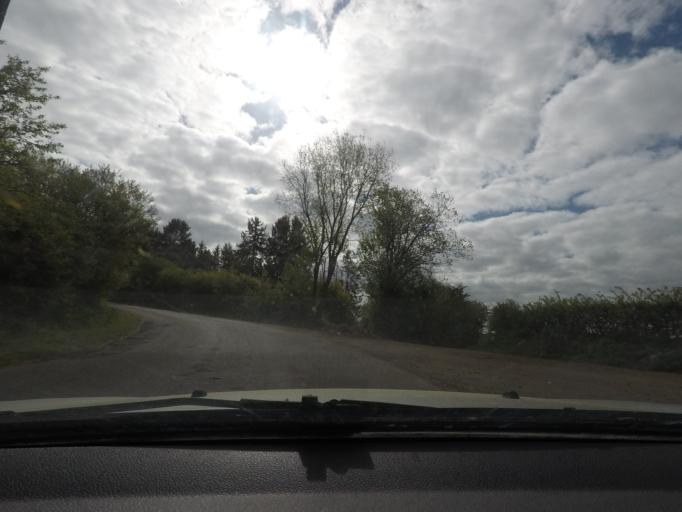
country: BE
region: Wallonia
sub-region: Province du Luxembourg
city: Habay-la-Vieille
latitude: 49.7142
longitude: 5.5823
